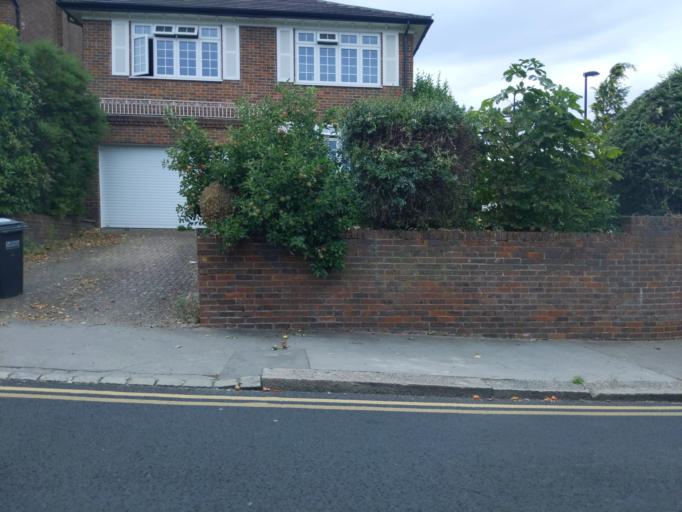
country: GB
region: England
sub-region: Greater London
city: South Croydon
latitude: 51.3591
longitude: -0.0857
